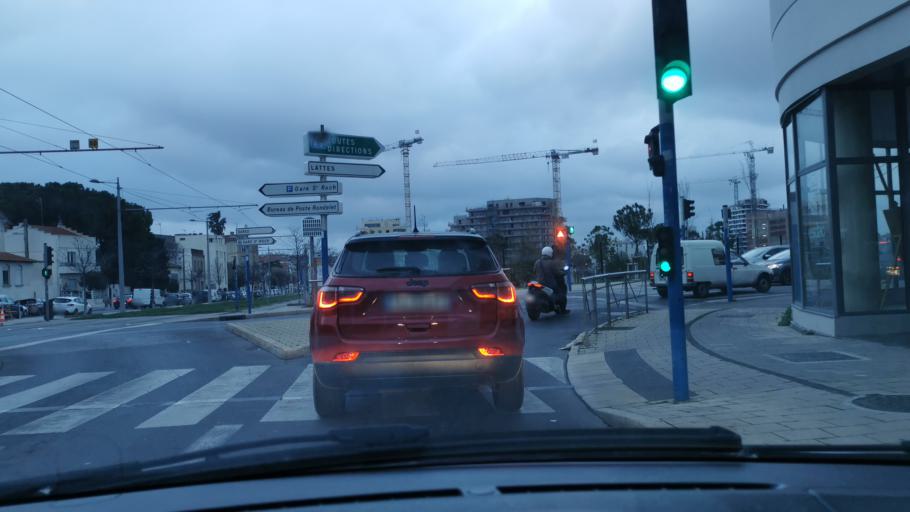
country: FR
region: Languedoc-Roussillon
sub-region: Departement de l'Herault
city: Montpellier
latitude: 43.5996
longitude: 3.8758
